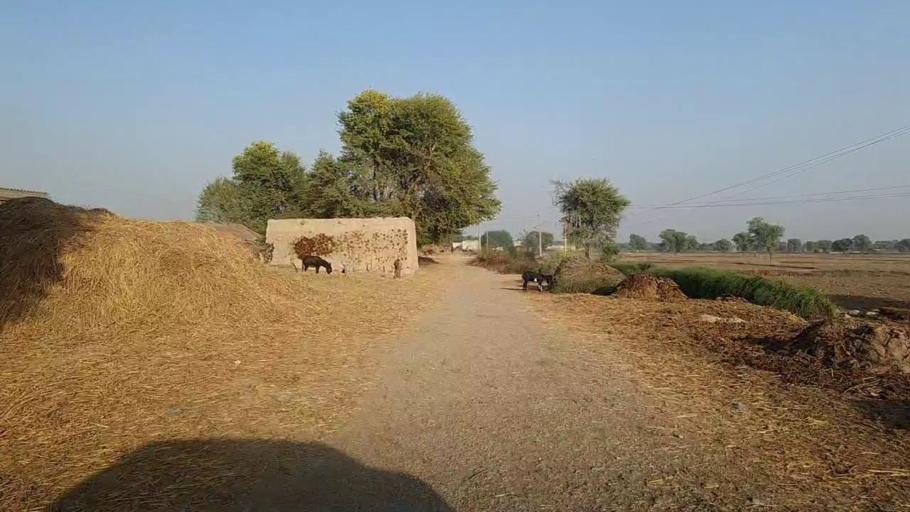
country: PK
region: Sindh
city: Kashmor
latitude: 28.4276
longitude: 69.4514
